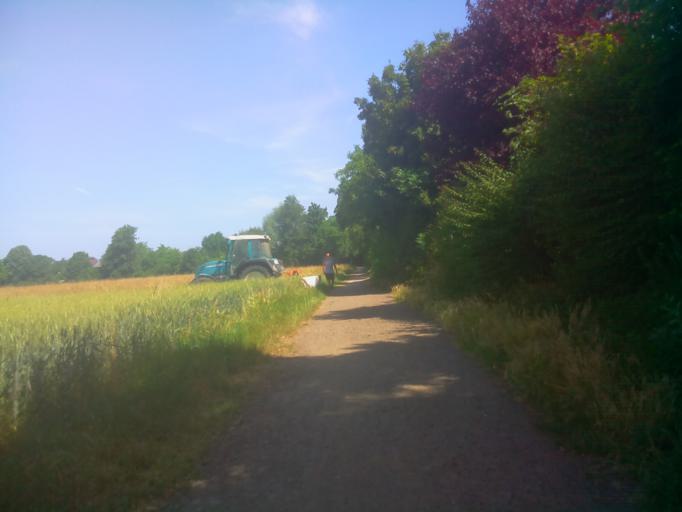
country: DE
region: Baden-Wuerttemberg
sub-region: Karlsruhe Region
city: Hemsbach
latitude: 49.5847
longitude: 8.6435
